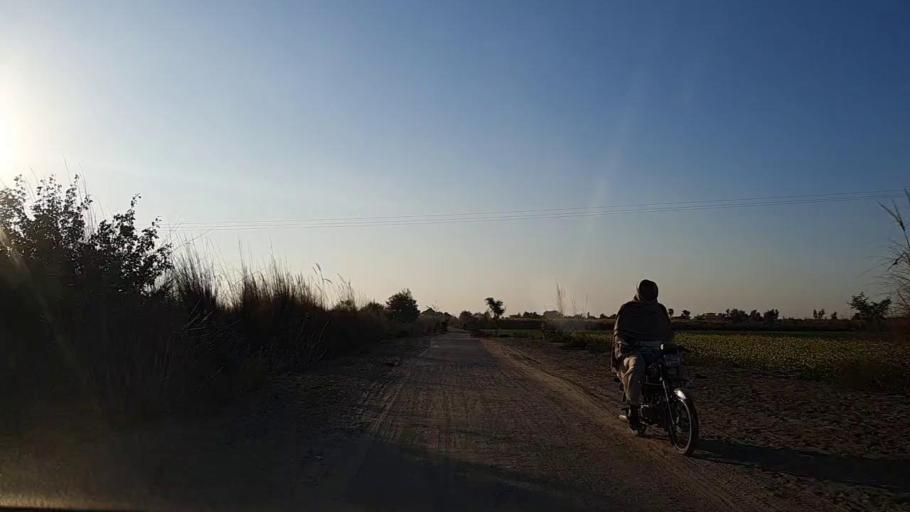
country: PK
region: Sindh
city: Khadro
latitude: 26.2791
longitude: 68.8181
